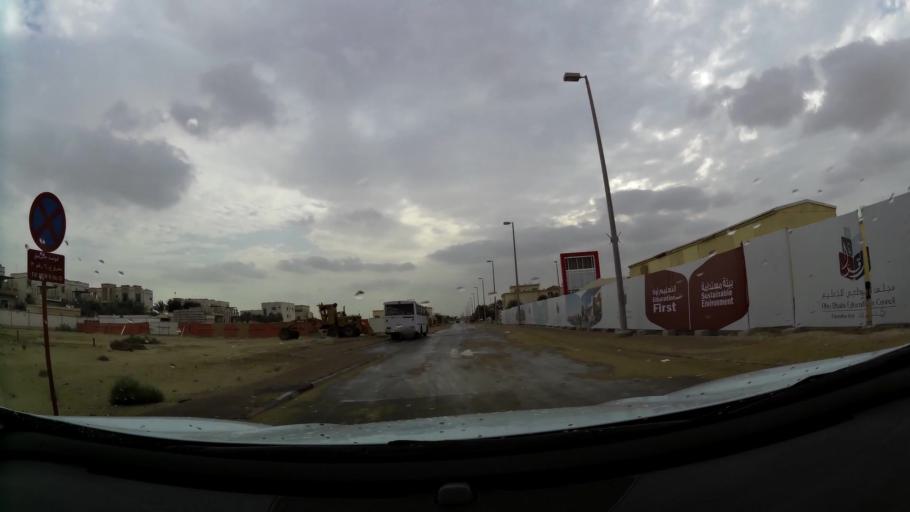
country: AE
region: Abu Dhabi
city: Abu Dhabi
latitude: 24.3539
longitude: 54.6235
